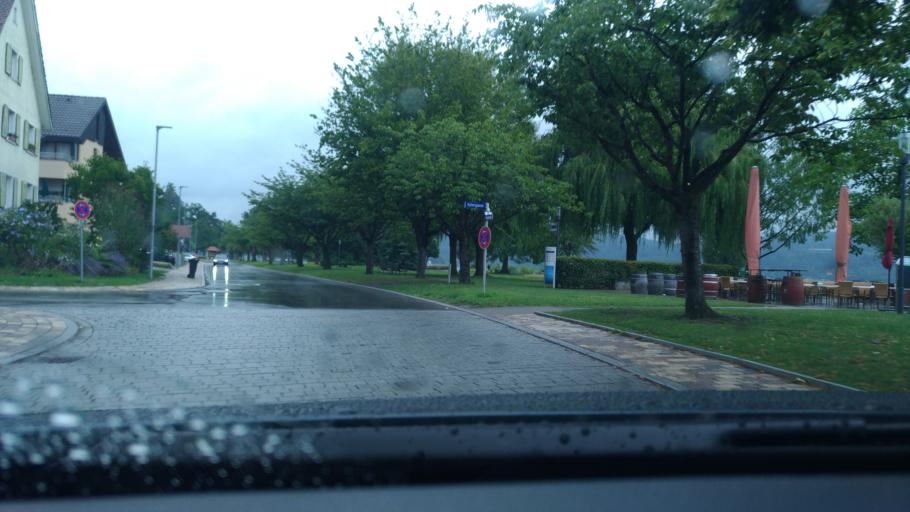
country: DE
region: Baden-Wuerttemberg
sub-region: Freiburg Region
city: Bodman-Ludwigshafen
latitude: 47.7987
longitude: 9.0415
